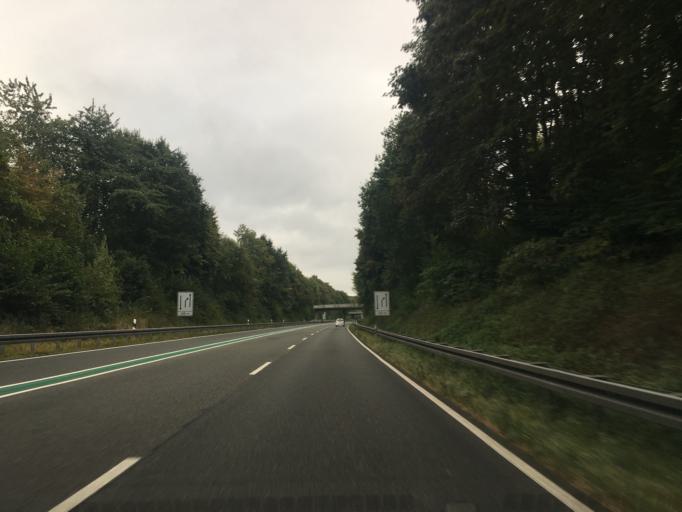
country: DE
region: North Rhine-Westphalia
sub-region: Regierungsbezirk Munster
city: Steinfurt
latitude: 52.1549
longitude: 7.3512
